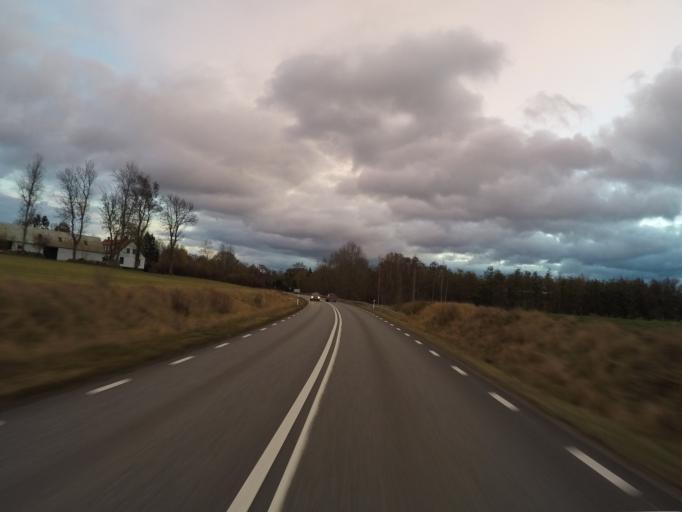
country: SE
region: Skane
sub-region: Kristianstads Kommun
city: Degeberga
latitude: 55.8998
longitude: 14.0709
